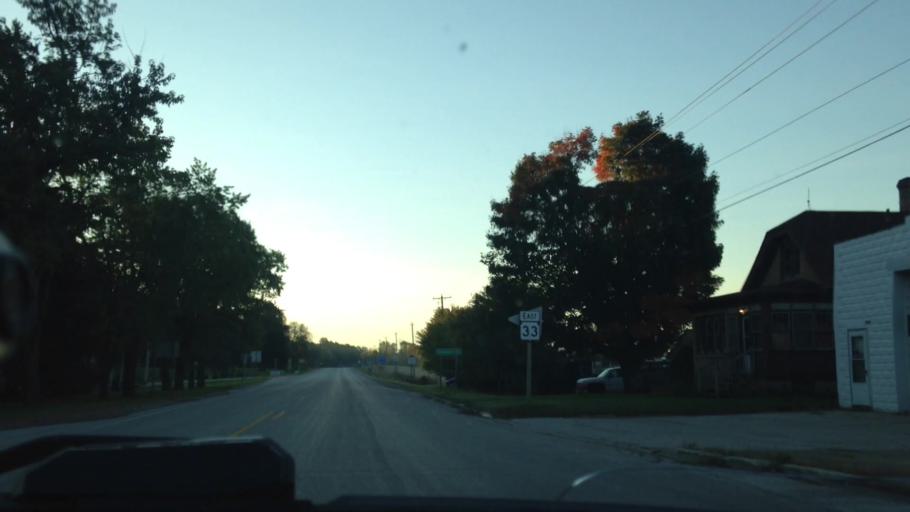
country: US
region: Wisconsin
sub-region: Washington County
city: Newburg
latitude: 43.4286
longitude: -88.0407
